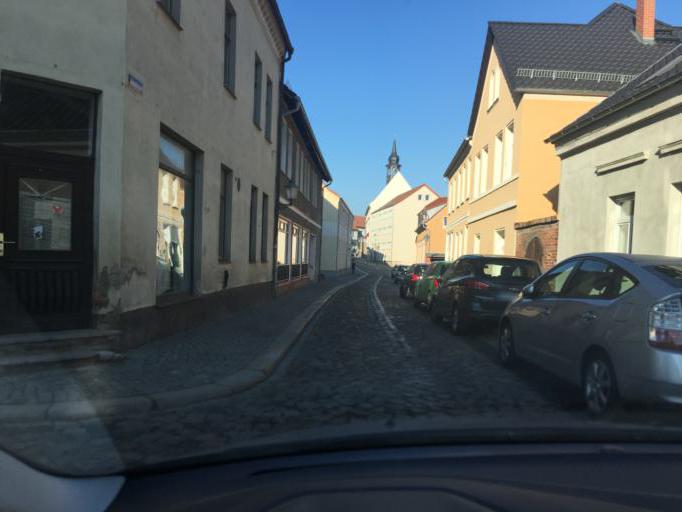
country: DE
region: Saxony-Anhalt
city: Wanzleben
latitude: 52.0612
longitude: 11.4425
